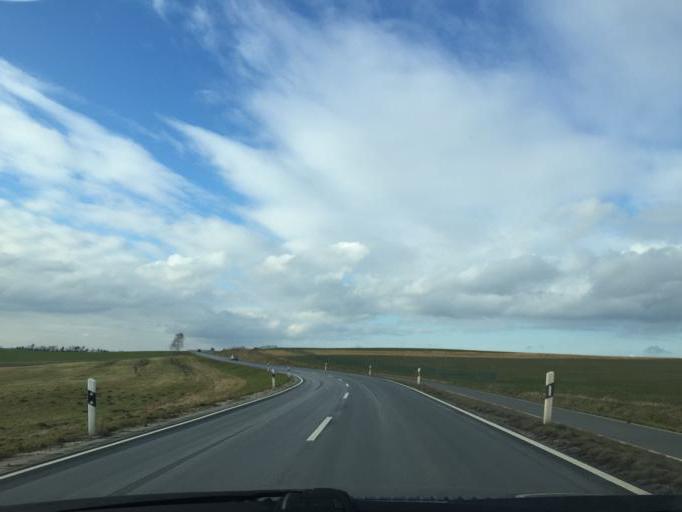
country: DE
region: Saxony
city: Wachau
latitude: 51.1653
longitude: 13.8723
